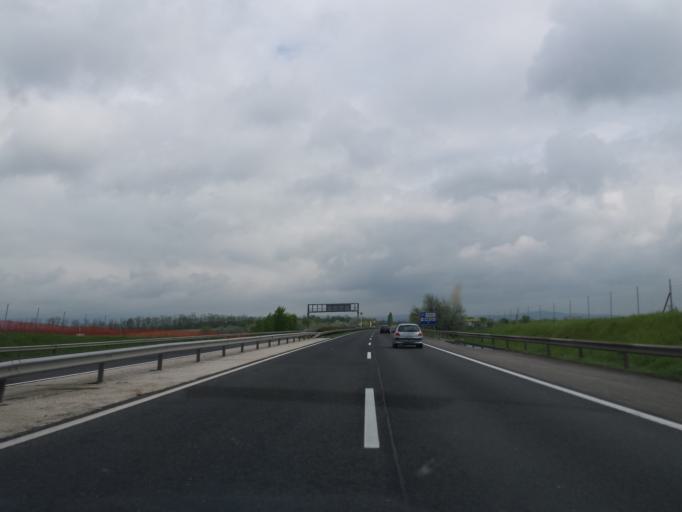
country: HU
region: Pest
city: Zsambek
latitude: 47.5110
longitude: 18.7286
